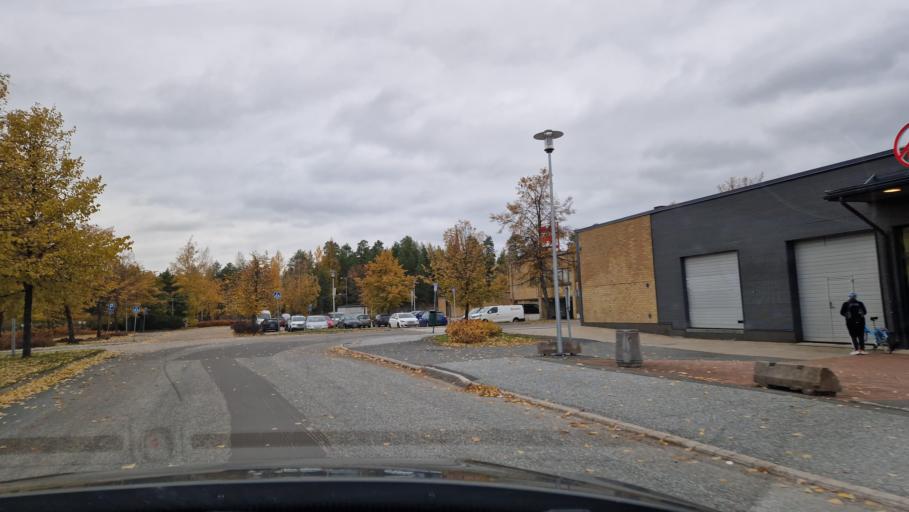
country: FI
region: Northern Savo
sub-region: Kuopio
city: Siilinjaervi
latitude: 63.0740
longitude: 27.6577
